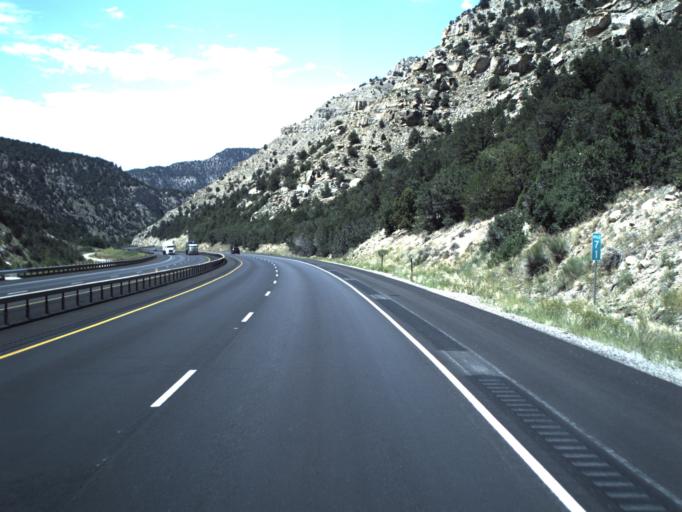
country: US
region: Utah
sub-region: Sevier County
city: Salina
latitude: 38.8908
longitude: -111.6144
